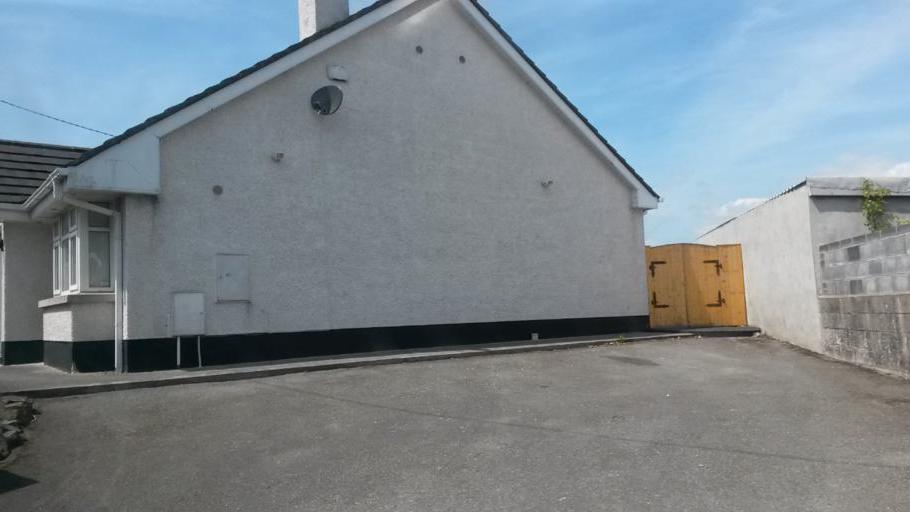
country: IE
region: Leinster
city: Lusk
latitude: 53.5288
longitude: -6.1667
